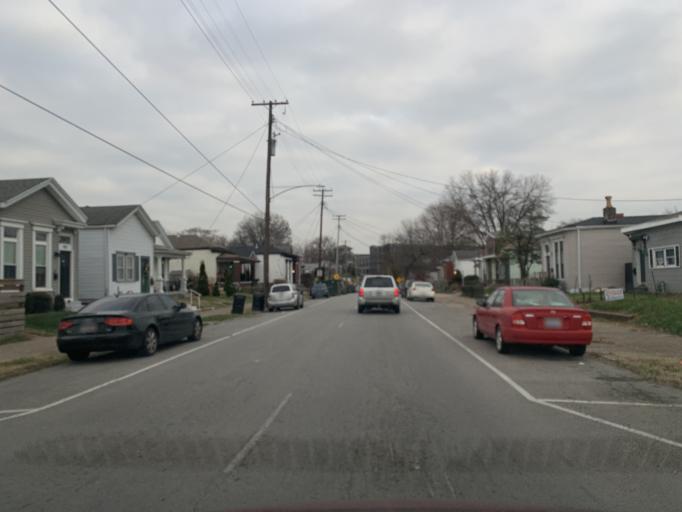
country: US
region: Kentucky
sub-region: Jefferson County
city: Louisville
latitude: 38.2331
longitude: -85.7392
